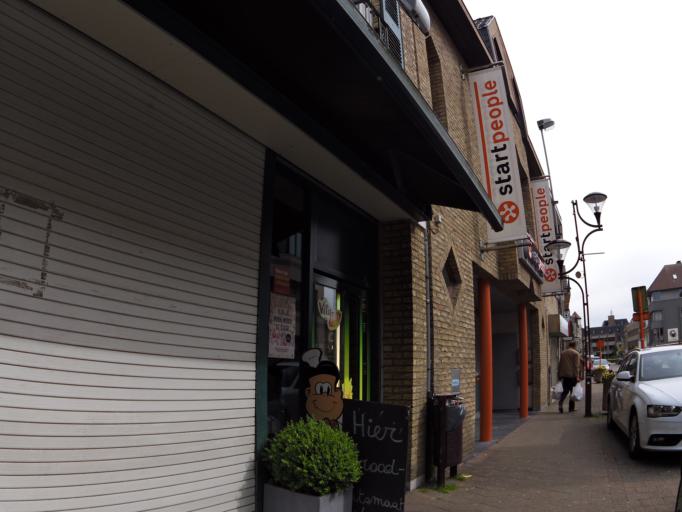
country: BE
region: Flanders
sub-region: Provincie West-Vlaanderen
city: Veurne
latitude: 51.0708
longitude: 2.6619
